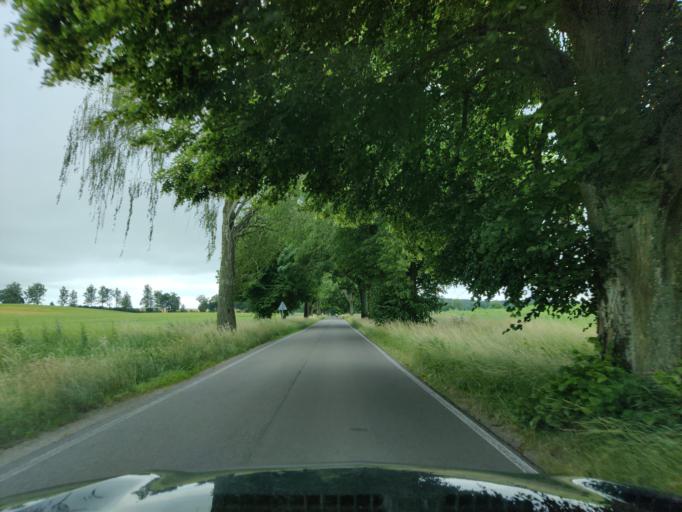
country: PL
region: Warmian-Masurian Voivodeship
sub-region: Powiat gizycki
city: Ryn
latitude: 53.9034
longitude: 21.5651
